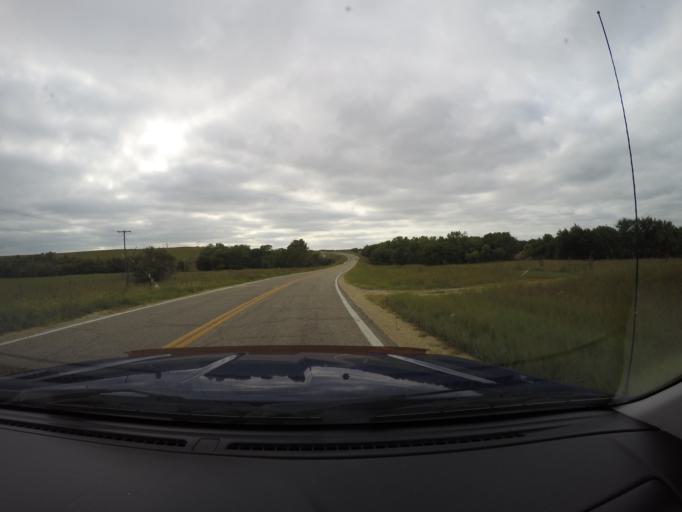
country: US
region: Kansas
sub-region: Dickinson County
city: Herington
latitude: 38.7978
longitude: -96.9282
